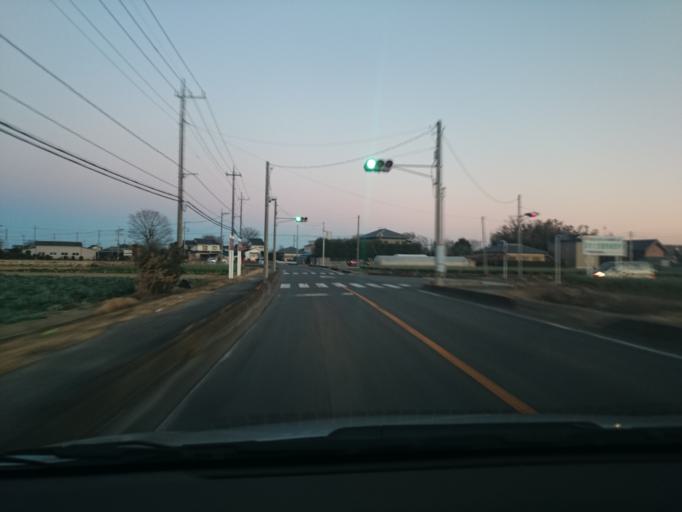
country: JP
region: Saitama
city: Fukayacho
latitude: 36.2265
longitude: 139.3238
